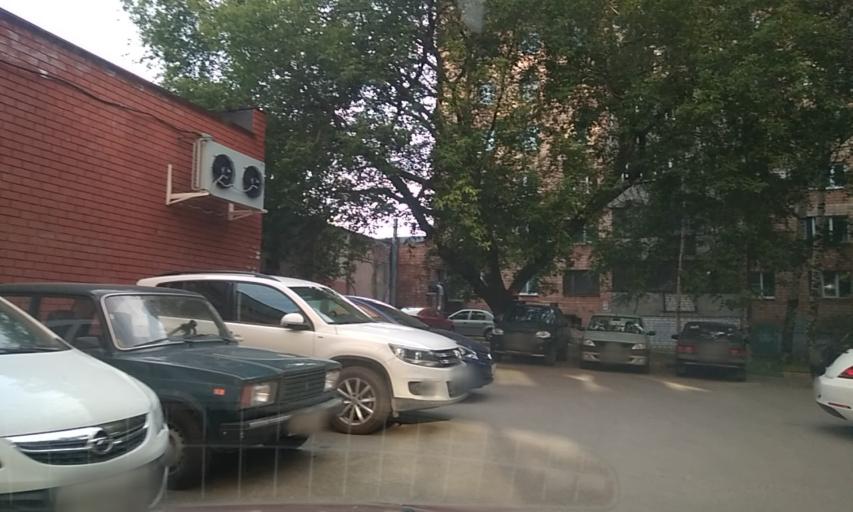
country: RU
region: Nizjnij Novgorod
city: Nizhniy Novgorod
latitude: 56.3169
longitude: 44.0069
